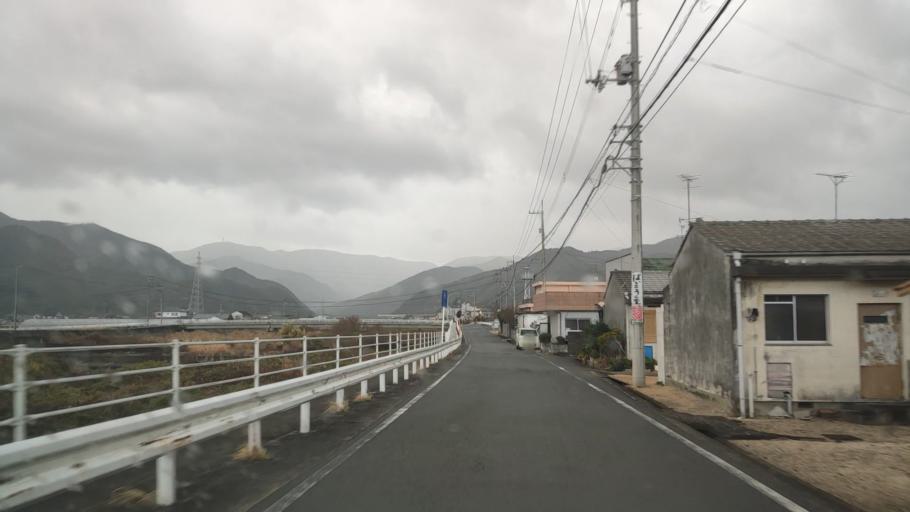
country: JP
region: Tokushima
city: Ishii
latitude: 34.2162
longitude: 134.4072
